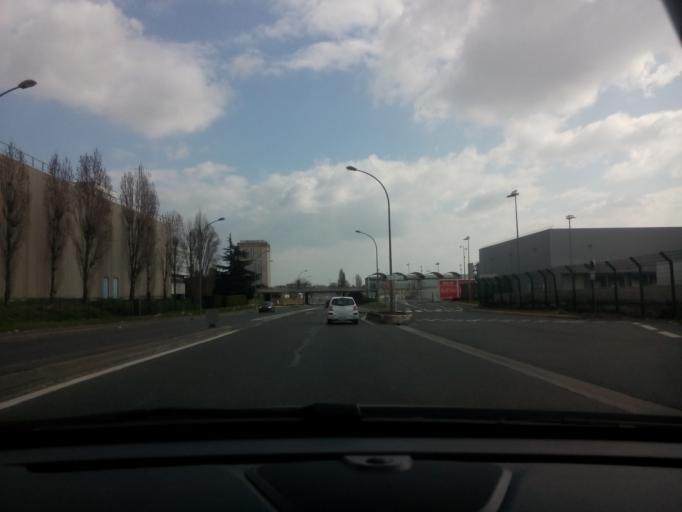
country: FR
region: Ile-de-France
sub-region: Departement du Val-de-Marne
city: Chevilly-Larue
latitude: 48.7602
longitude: 2.3420
